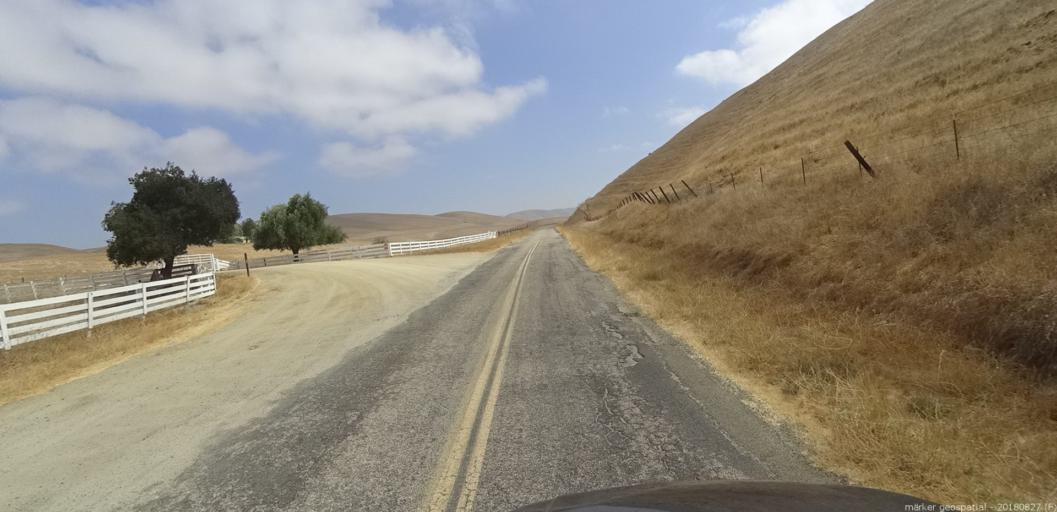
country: US
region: California
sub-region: Monterey County
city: King City
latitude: 36.2269
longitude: -121.0641
